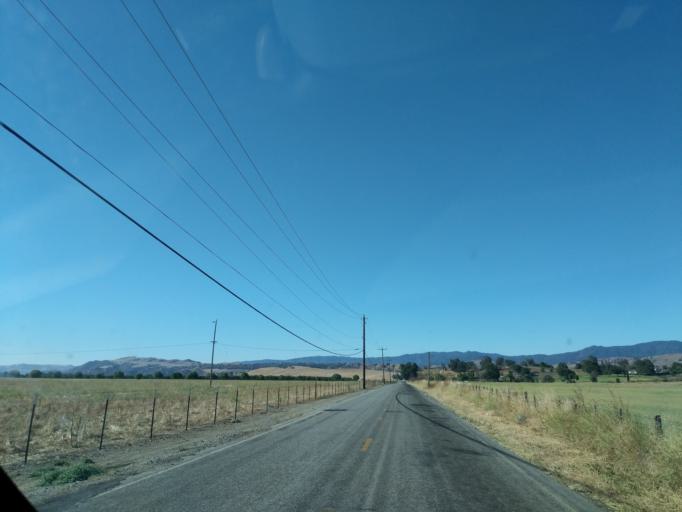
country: US
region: California
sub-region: San Benito County
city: Ridgemark
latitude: 36.8154
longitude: -121.3454
